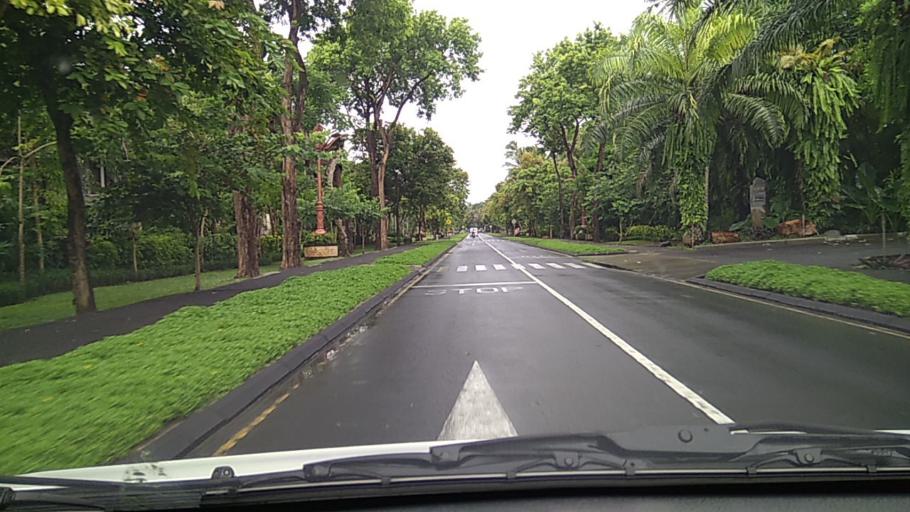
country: ID
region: Bali
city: Bualu
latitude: -8.7920
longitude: 115.2273
